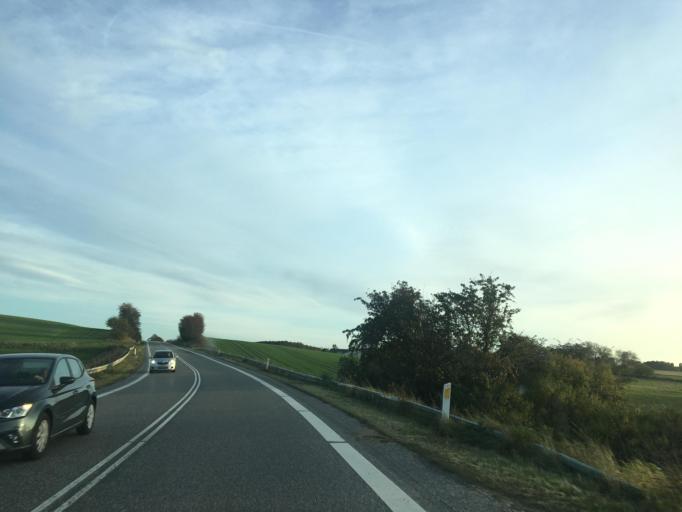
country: DK
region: Zealand
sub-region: Odsherred Kommune
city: Asnaes
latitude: 55.8238
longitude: 11.5734
